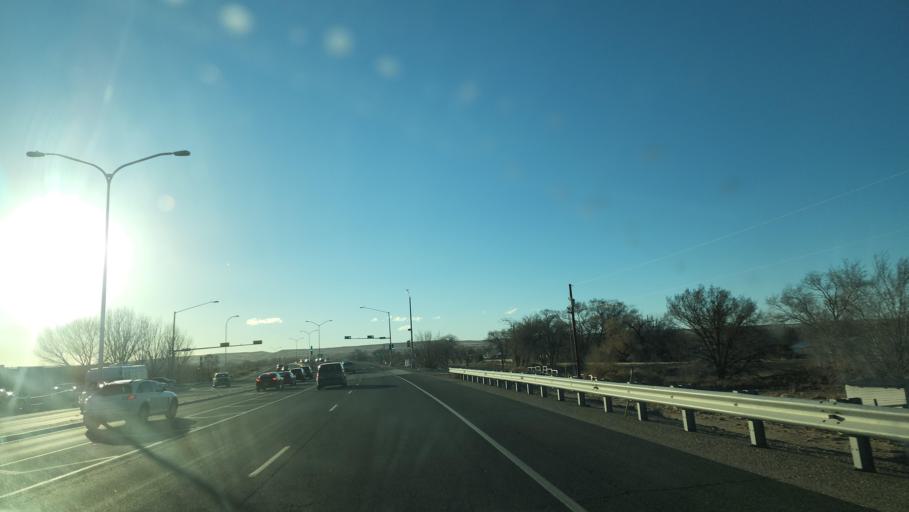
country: US
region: New Mexico
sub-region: Bernalillo County
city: South Valley
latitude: 35.0277
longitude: -106.7082
